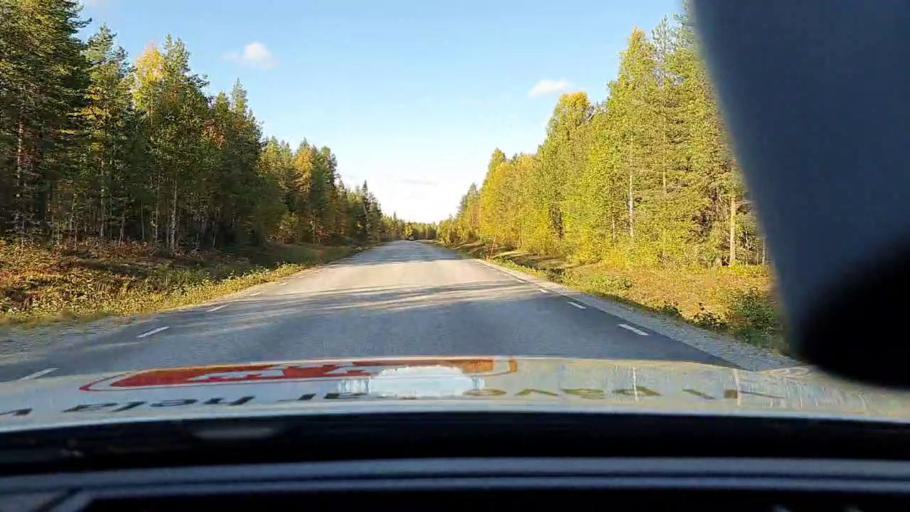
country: SE
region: Norrbotten
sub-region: Pitea Kommun
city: Norrfjarden
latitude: 65.4974
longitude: 21.4753
